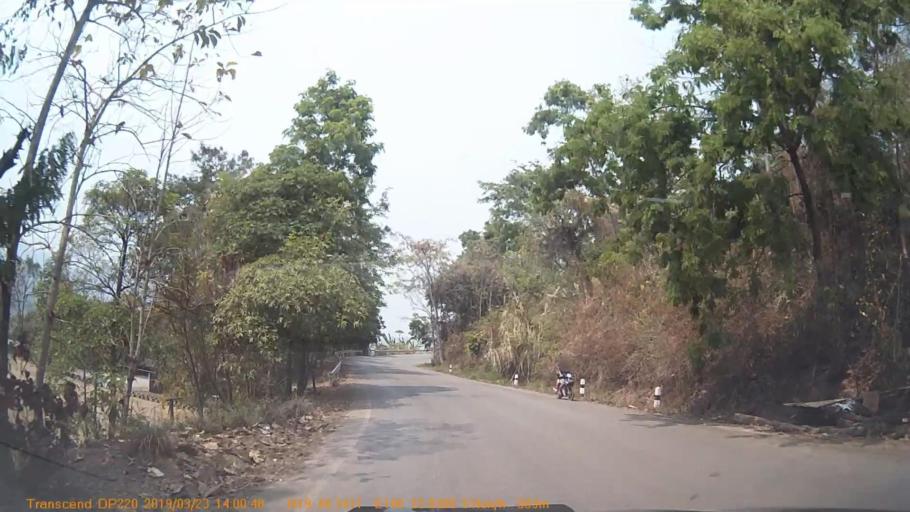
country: TH
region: Chiang Rai
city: Khun Tan
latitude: 19.8225
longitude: 100.3672
